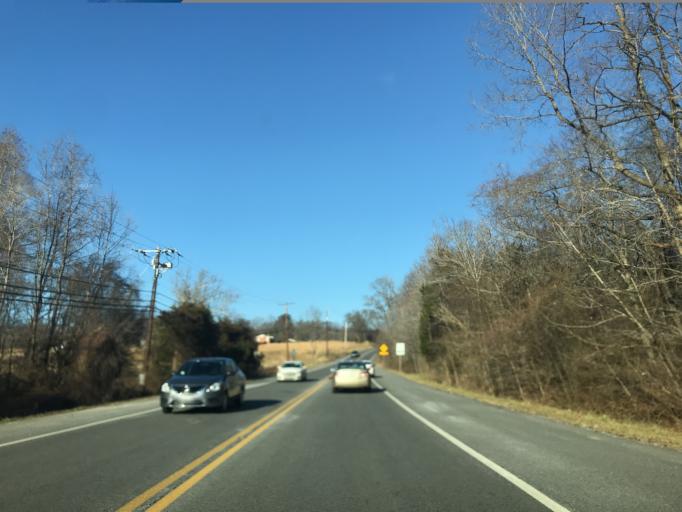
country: US
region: Maryland
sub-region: Prince George's County
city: Friendly
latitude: 38.7074
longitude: -76.9653
